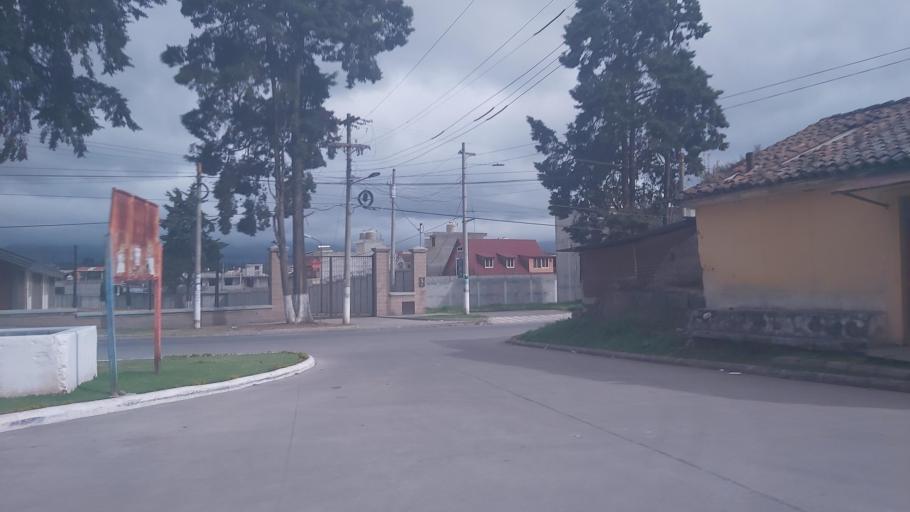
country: GT
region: Quetzaltenango
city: Quetzaltenango
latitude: 14.8275
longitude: -91.5313
